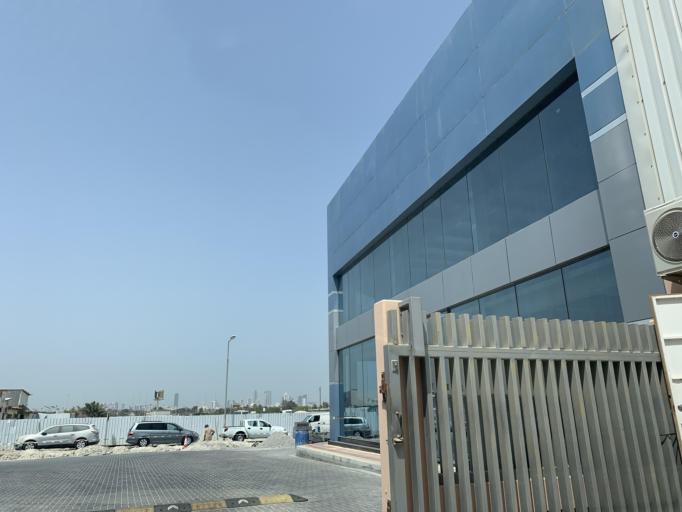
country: BH
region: Northern
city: Madinat `Isa
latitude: 26.1922
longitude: 50.5412
